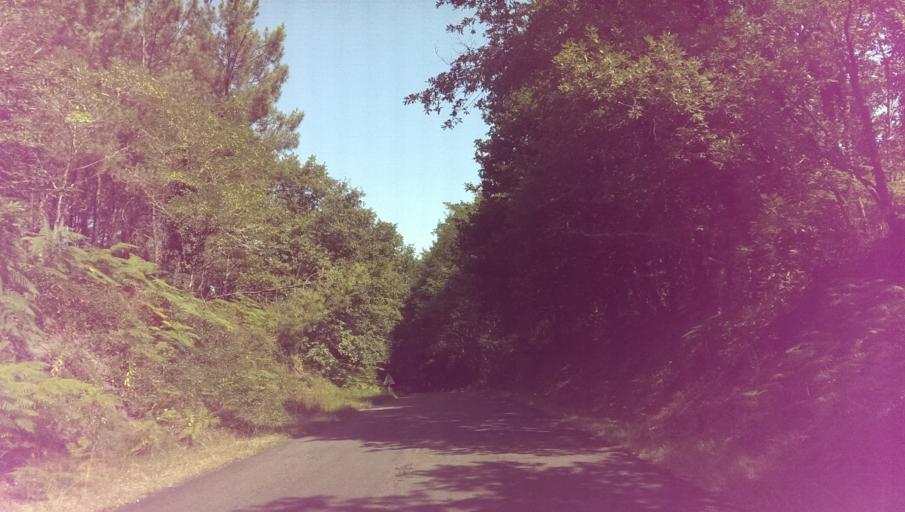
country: FR
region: Aquitaine
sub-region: Departement des Landes
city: Sarbazan
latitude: 44.0403
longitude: -0.1872
